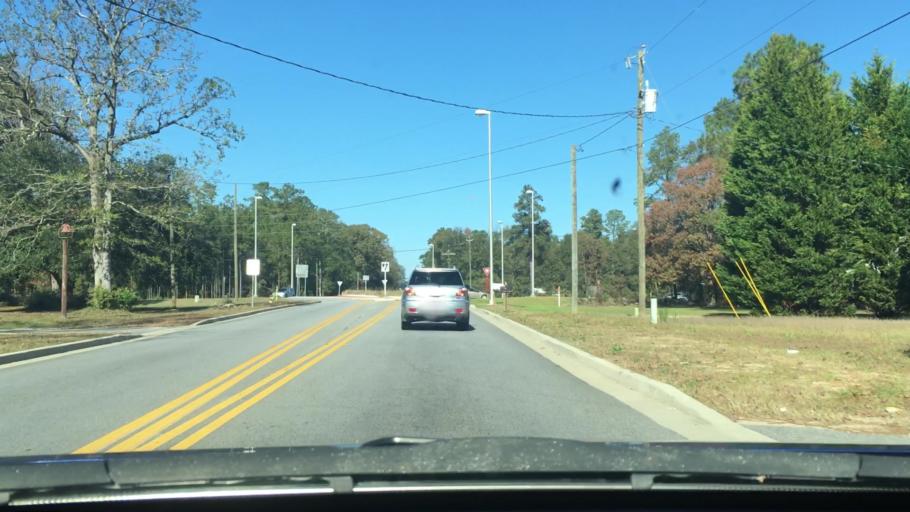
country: US
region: South Carolina
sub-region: Sumter County
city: South Sumter
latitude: 33.8876
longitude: -80.3647
